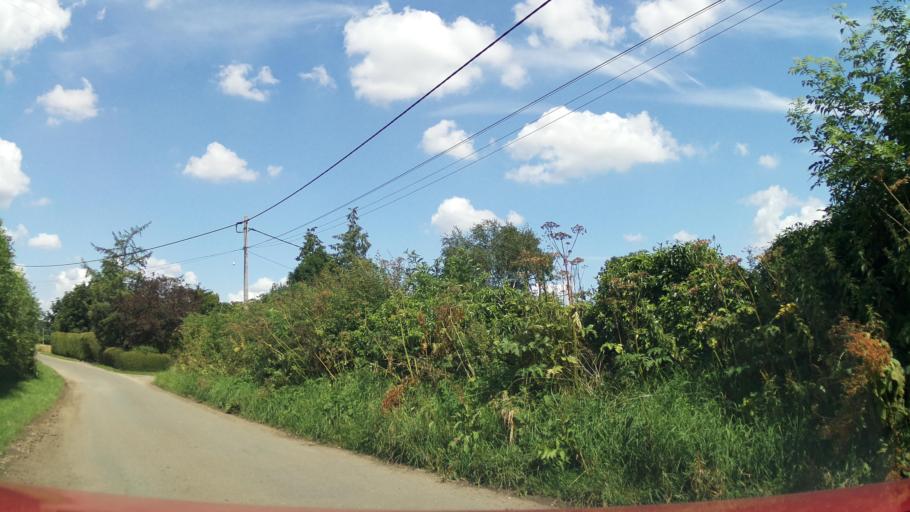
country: GB
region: England
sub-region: West Berkshire
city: Farnborough
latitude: 51.5098
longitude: -1.3817
